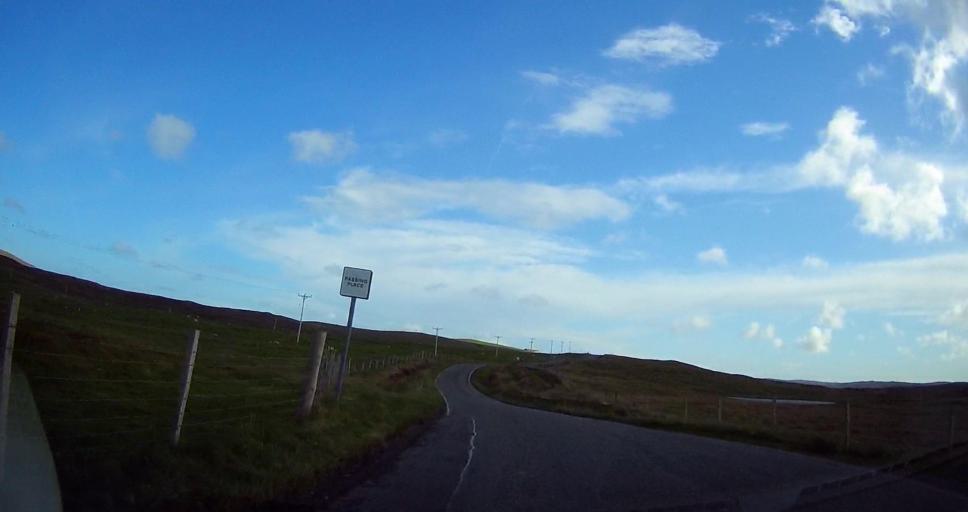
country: GB
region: Scotland
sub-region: Shetland Islands
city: Shetland
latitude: 60.3664
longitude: -1.1416
